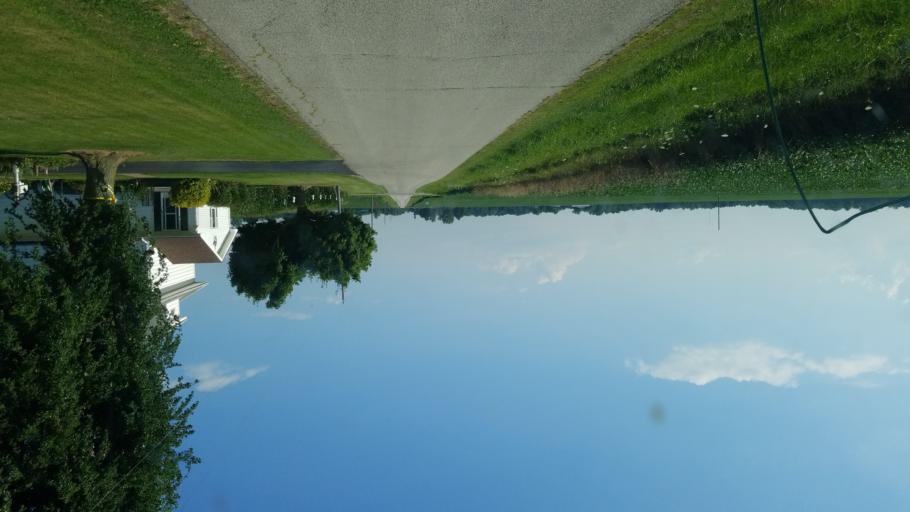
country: US
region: Ohio
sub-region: Crawford County
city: Bucyrus
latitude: 40.8034
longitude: -83.0738
